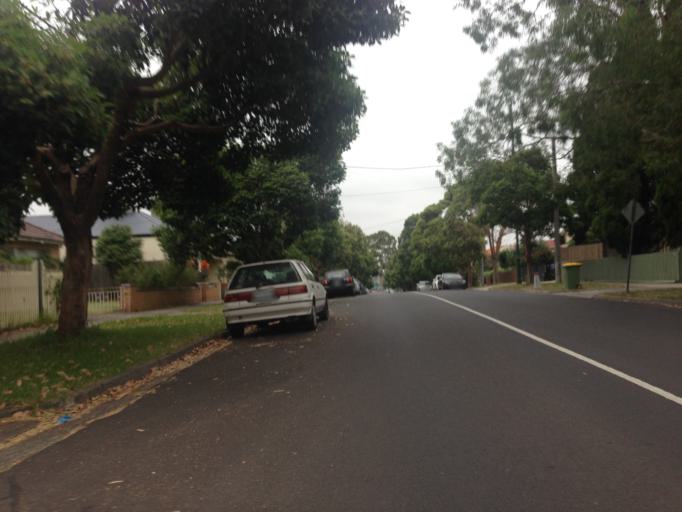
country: AU
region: Victoria
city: Thornbury
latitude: -37.7513
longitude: 145.0066
